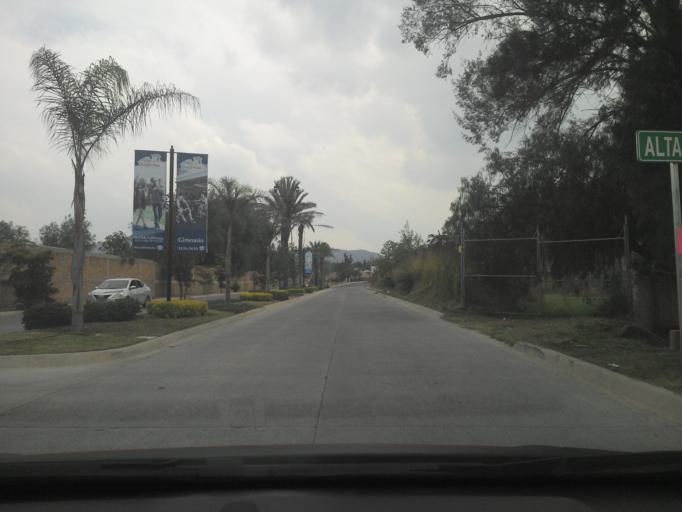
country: MX
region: Jalisco
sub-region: Tlajomulco de Zuniga
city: Lomas de San Agustin
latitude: 20.5310
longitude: -103.4750
